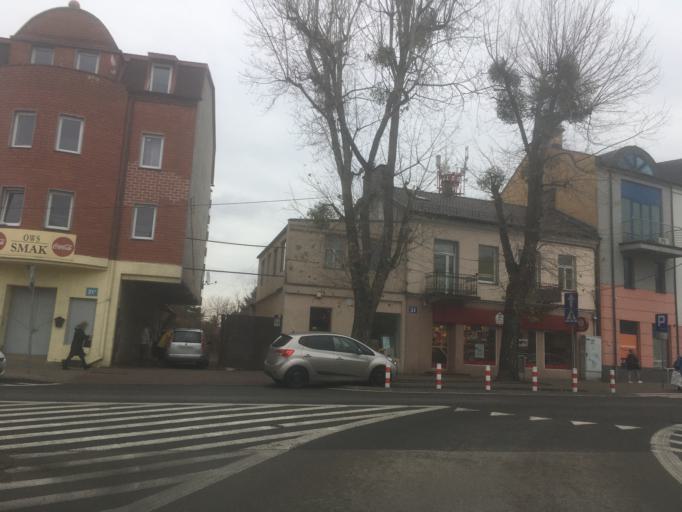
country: PL
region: Masovian Voivodeship
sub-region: Powiat piaseczynski
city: Piaseczno
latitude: 52.0700
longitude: 21.0267
